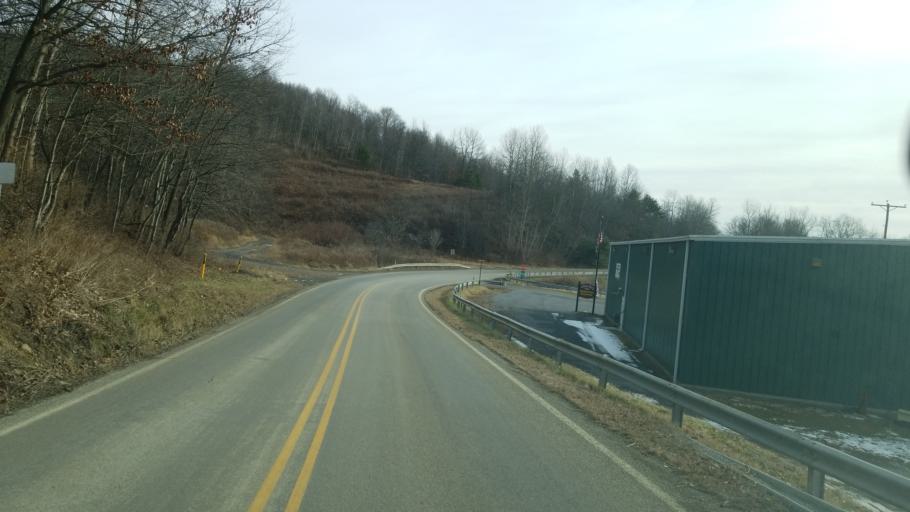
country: US
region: Pennsylvania
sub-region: Jefferson County
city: Punxsutawney
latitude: 40.9617
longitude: -78.9907
